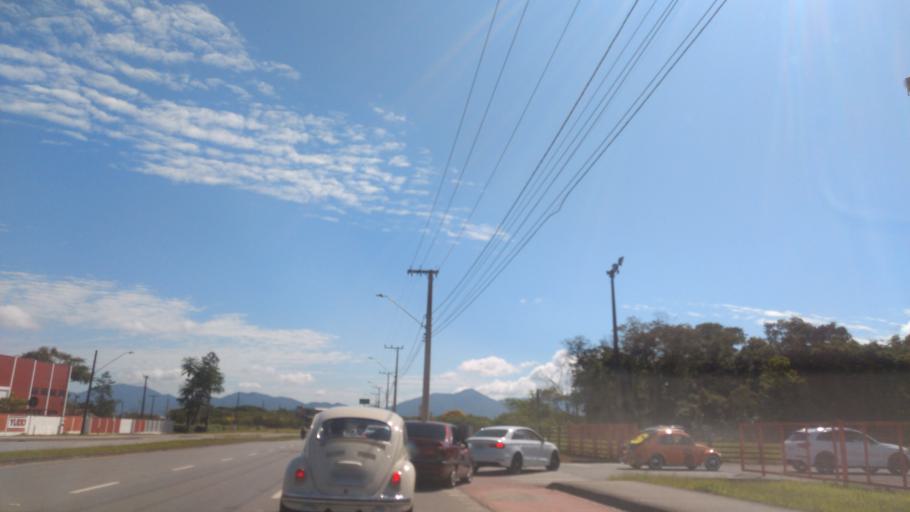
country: BR
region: Santa Catarina
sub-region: Joinville
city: Joinville
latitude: -26.2284
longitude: -48.8049
